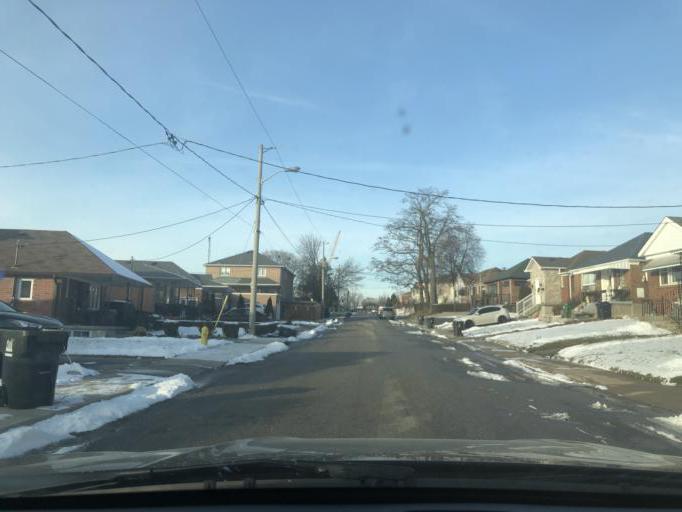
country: CA
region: Ontario
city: Toronto
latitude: 43.6941
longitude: -79.4715
